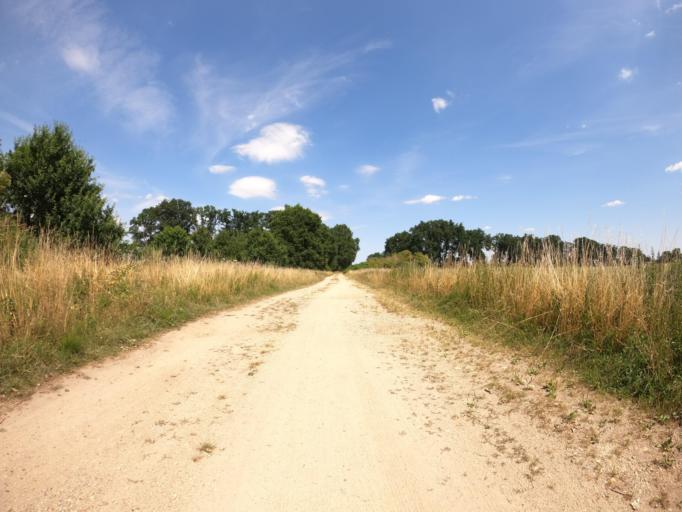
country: DE
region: Brandenburg
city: Mittenwalde
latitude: 53.2938
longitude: 13.5622
